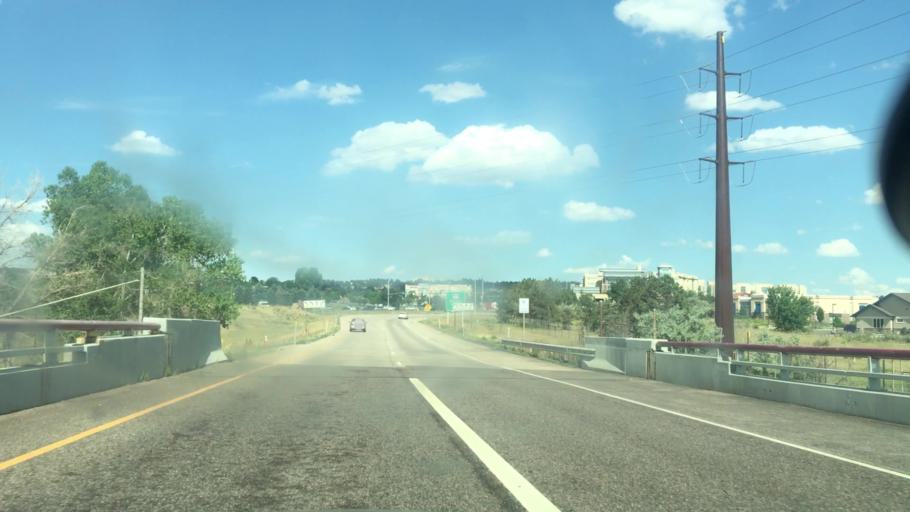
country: US
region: Colorado
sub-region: Douglas County
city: Stonegate
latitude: 39.5495
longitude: -104.7787
